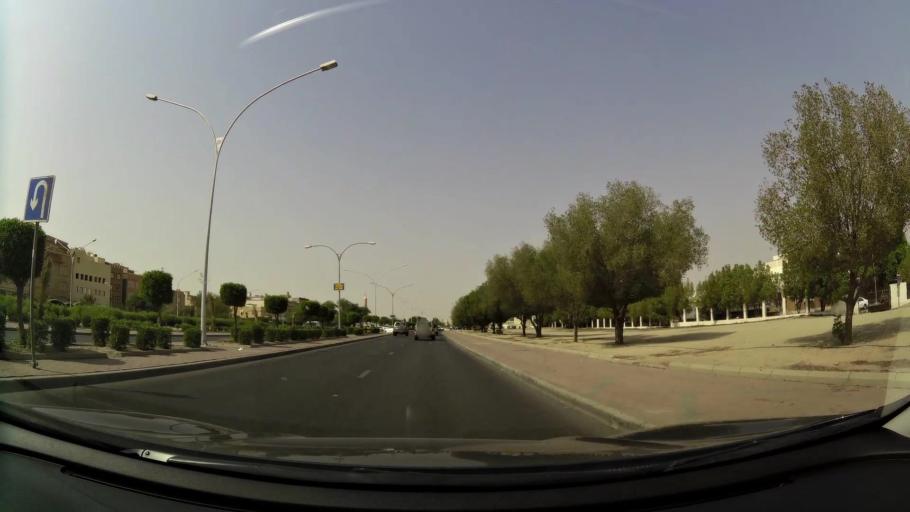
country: KW
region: Muhafazat al Jahra'
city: Al Jahra'
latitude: 29.3387
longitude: 47.6928
